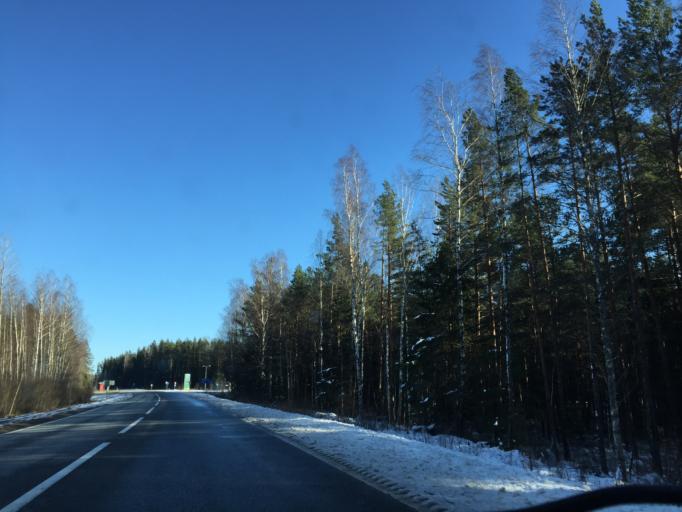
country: LV
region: Dundaga
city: Dundaga
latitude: 57.2480
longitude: 22.1691
